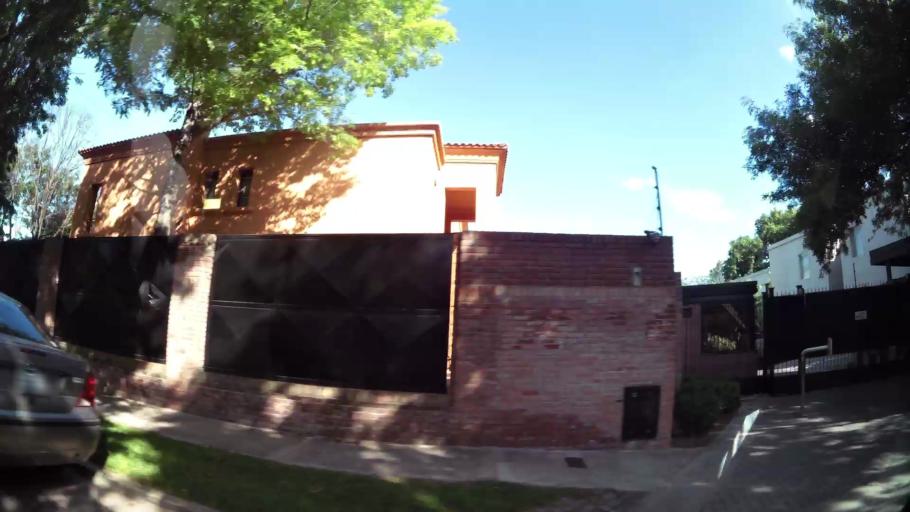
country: AR
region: Buenos Aires
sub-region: Partido de San Isidro
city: San Isidro
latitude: -34.4853
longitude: -58.5652
